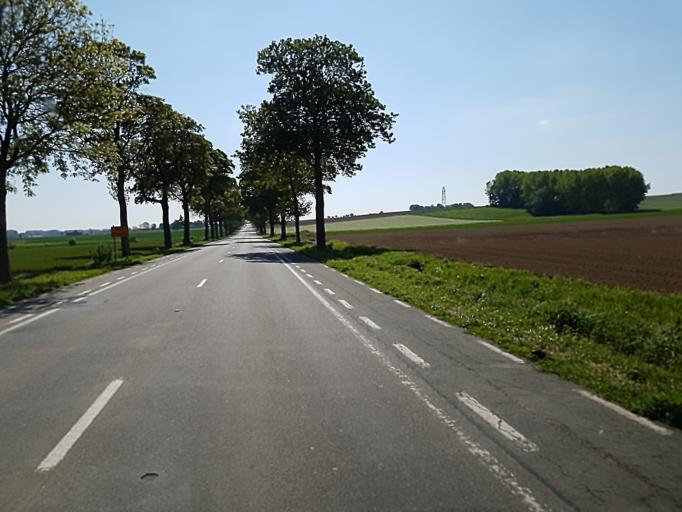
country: BE
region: Wallonia
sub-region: Province du Hainaut
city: Chievres
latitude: 50.6012
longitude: 3.8184
